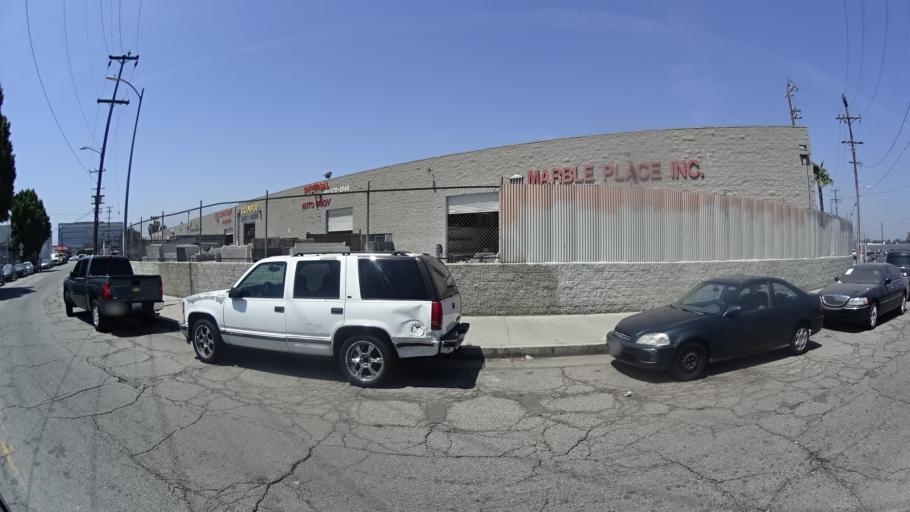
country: US
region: California
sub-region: Los Angeles County
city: Van Nuys
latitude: 34.2115
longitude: -118.4495
